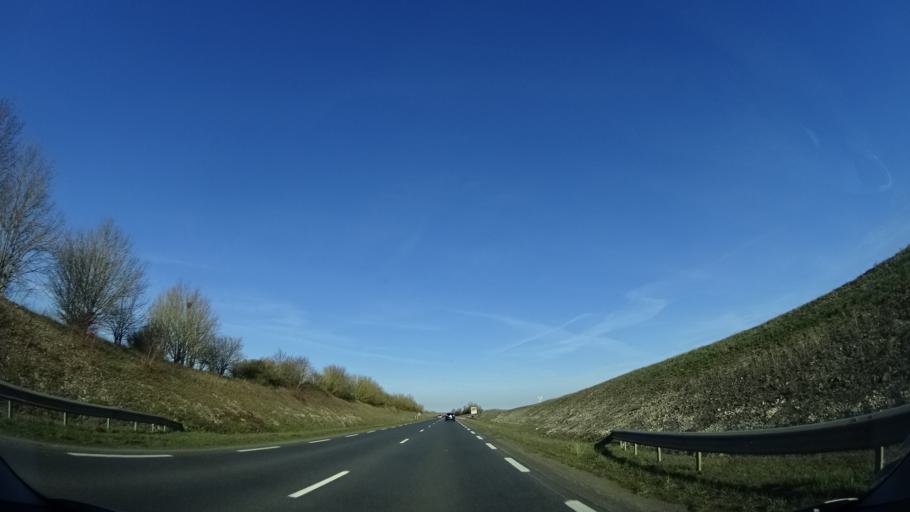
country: FR
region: Poitou-Charentes
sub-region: Departement de la Vienne
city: Neuville-de-Poitou
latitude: 46.7104
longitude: 0.2289
